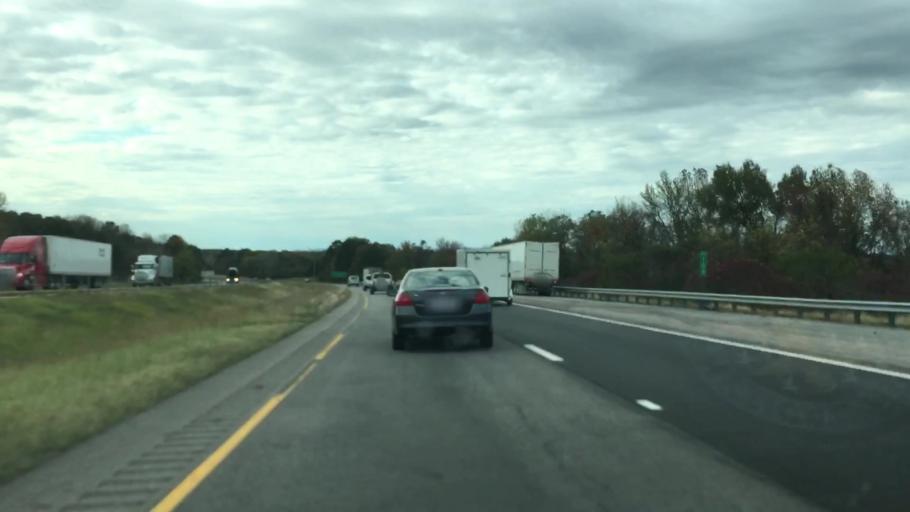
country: US
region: Arkansas
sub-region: Conway County
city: Morrilton
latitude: 35.1730
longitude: -92.7004
